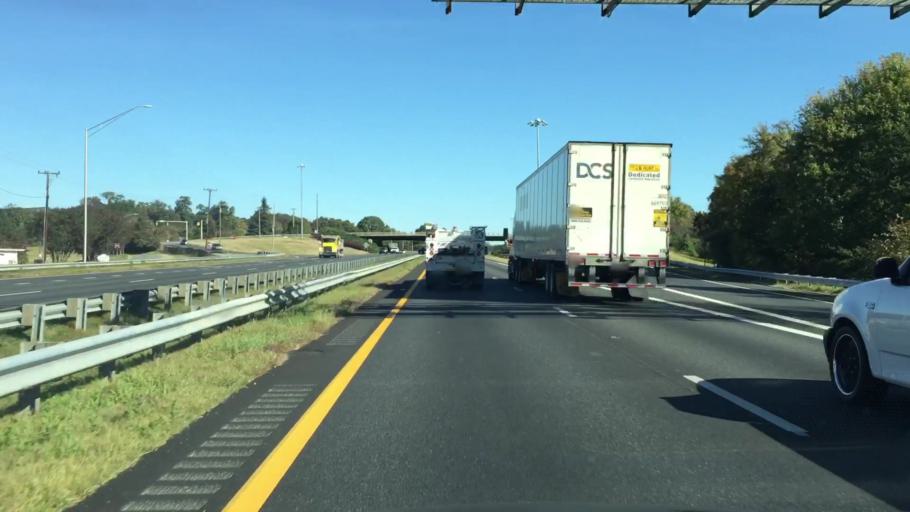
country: US
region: North Carolina
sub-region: Guilford County
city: Greensboro
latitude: 36.1100
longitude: -79.7588
